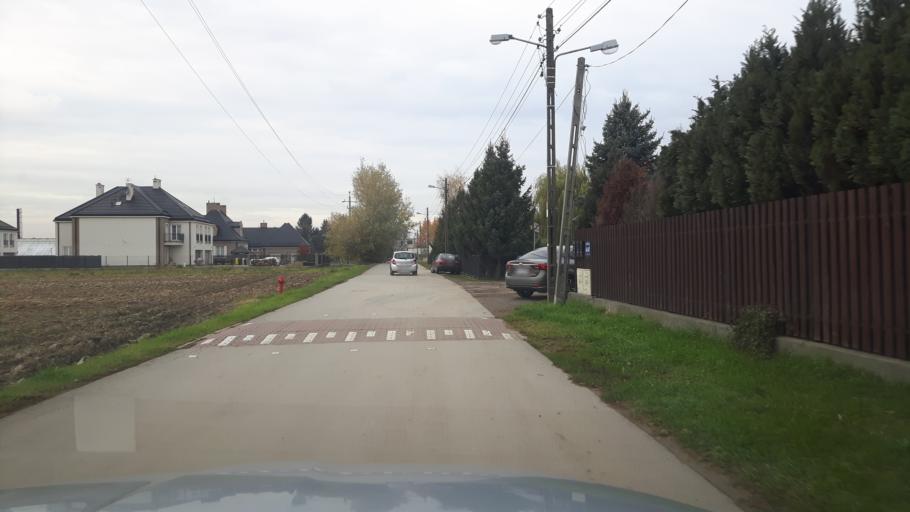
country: PL
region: Masovian Voivodeship
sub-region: Warszawa
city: Wilanow
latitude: 52.1595
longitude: 21.1266
